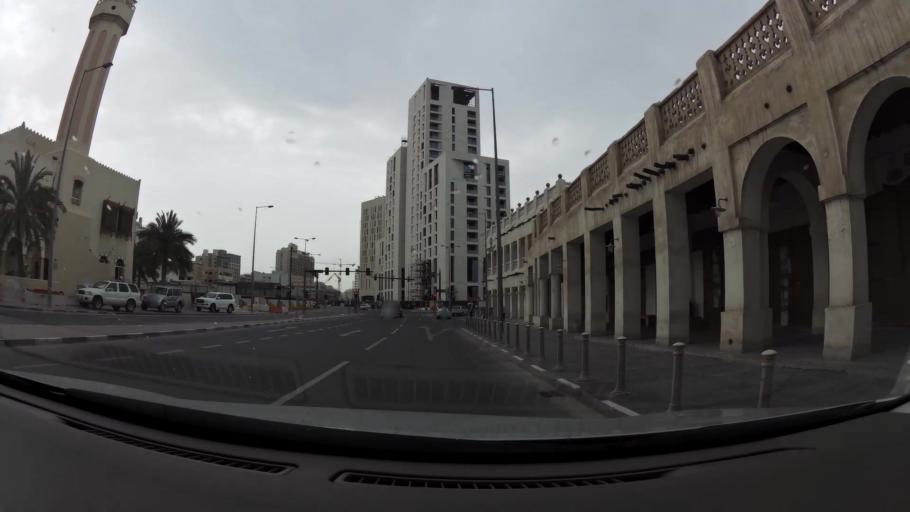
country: QA
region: Baladiyat ad Dawhah
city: Doha
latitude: 25.2858
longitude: 51.5318
